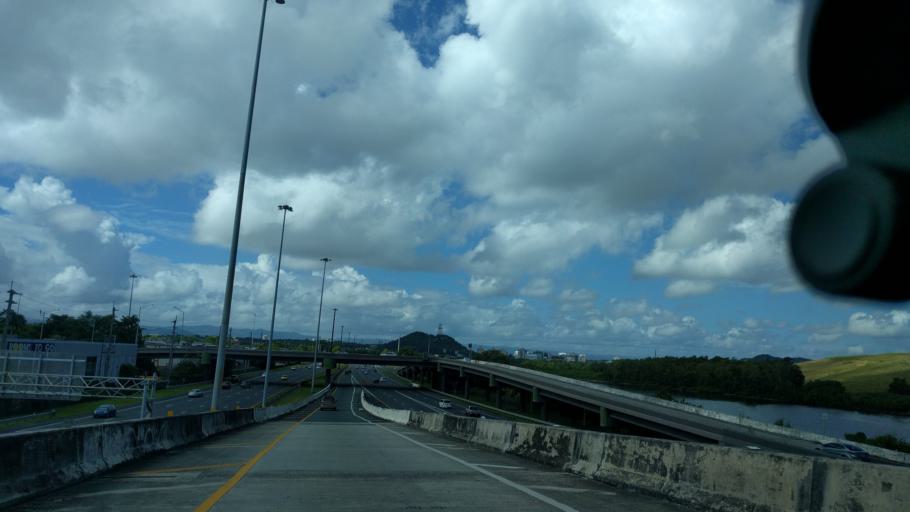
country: PR
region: Catano
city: Catano
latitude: 18.4272
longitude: -66.0770
